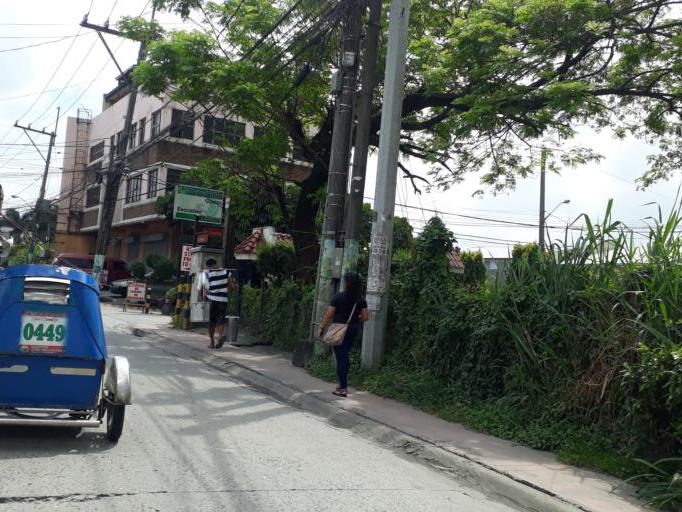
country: PH
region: Calabarzon
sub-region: Province of Rizal
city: Valenzuela
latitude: 14.7030
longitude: 121.0017
